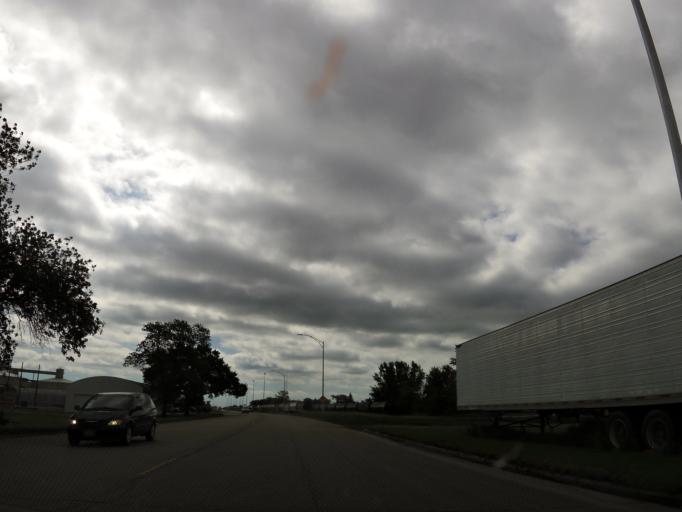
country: US
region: Minnesota
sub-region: Polk County
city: East Grand Forks
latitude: 47.9266
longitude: -97.0141
